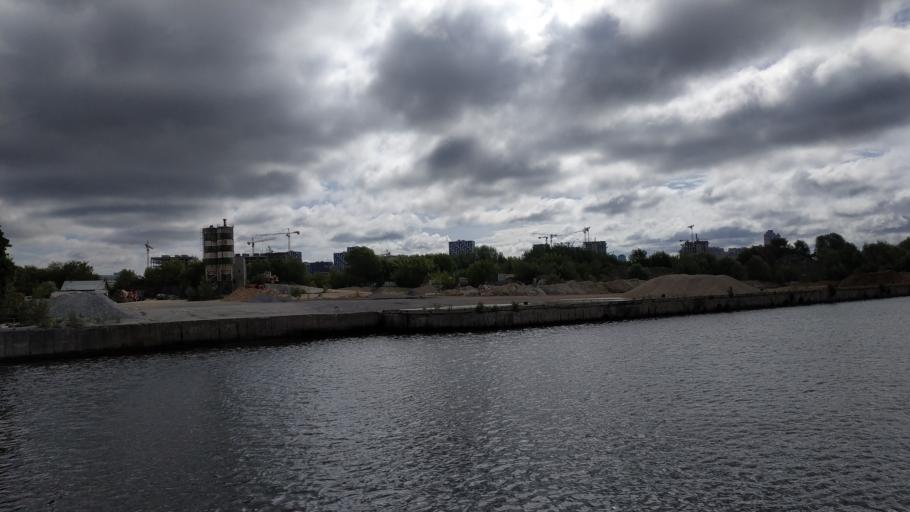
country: RU
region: Moscow
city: Strogino
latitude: 55.8215
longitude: 37.4130
